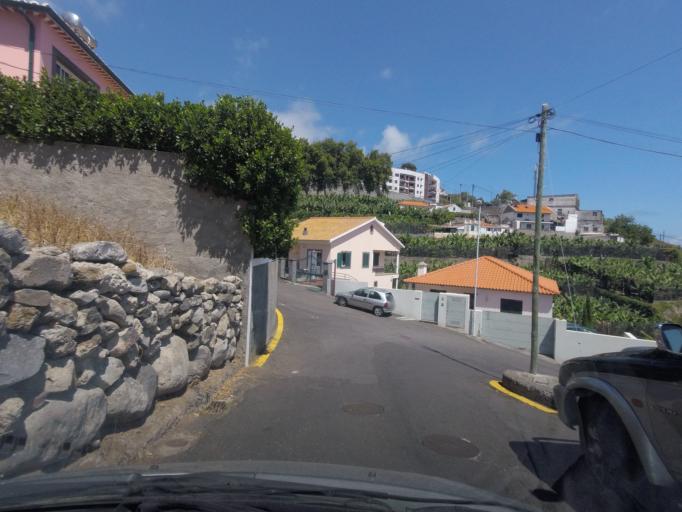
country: PT
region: Madeira
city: Camara de Lobos
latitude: 32.6445
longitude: -16.9567
